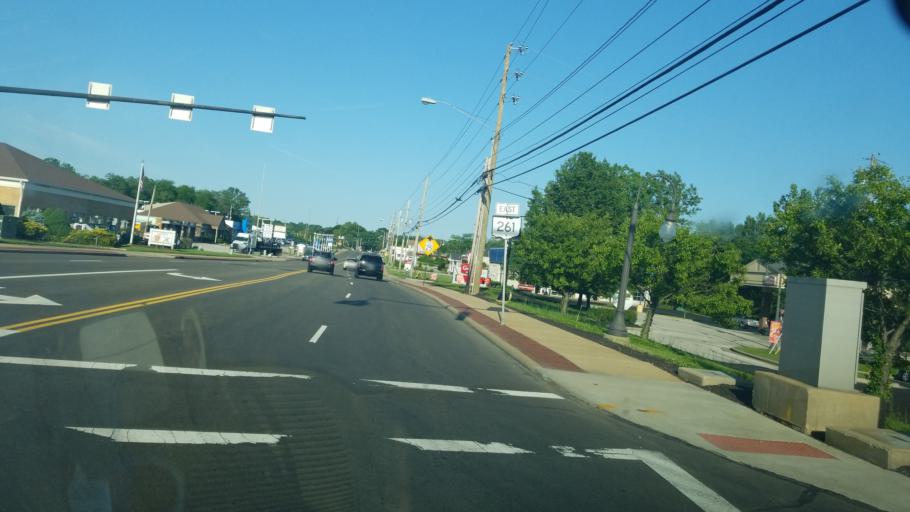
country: US
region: Ohio
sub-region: Summit County
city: Tallmadge
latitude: 41.1015
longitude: -81.4499
